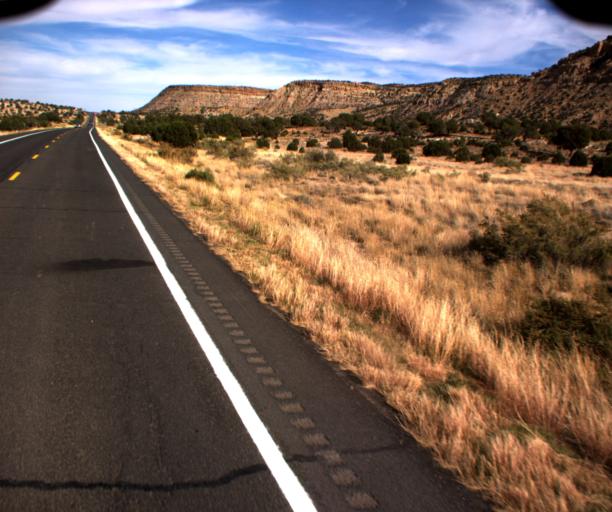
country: US
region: Arizona
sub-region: Navajo County
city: Kayenta
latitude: 36.6773
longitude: -110.3924
